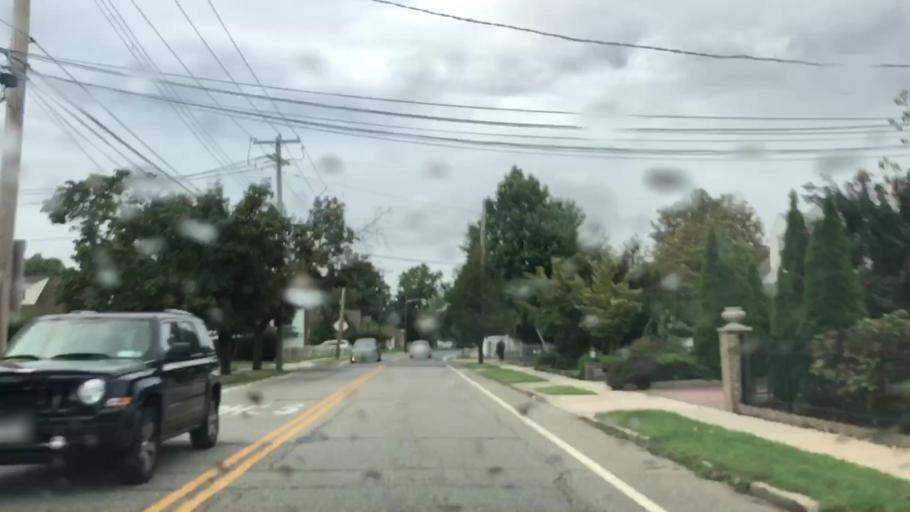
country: US
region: New York
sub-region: Nassau County
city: Stewart Manor
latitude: 40.7123
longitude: -73.6896
